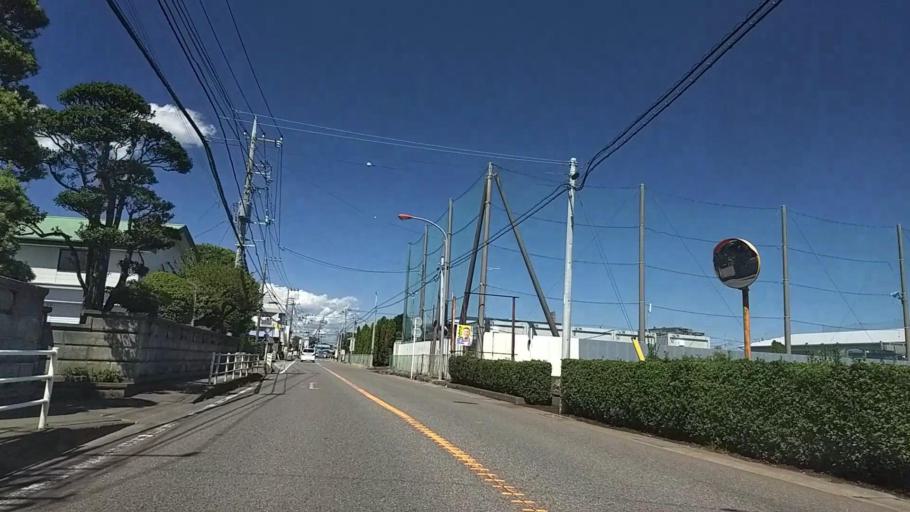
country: JP
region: Tokyo
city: Hachioji
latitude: 35.5674
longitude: 139.3225
